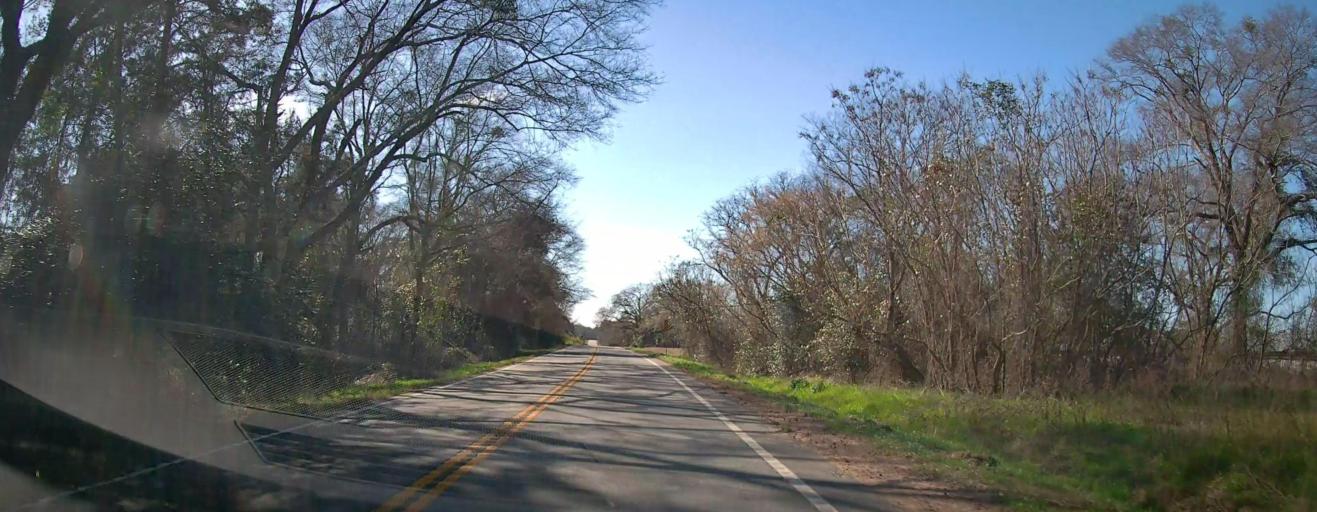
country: US
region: Georgia
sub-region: Macon County
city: Oglethorpe
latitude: 32.3516
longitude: -84.1578
